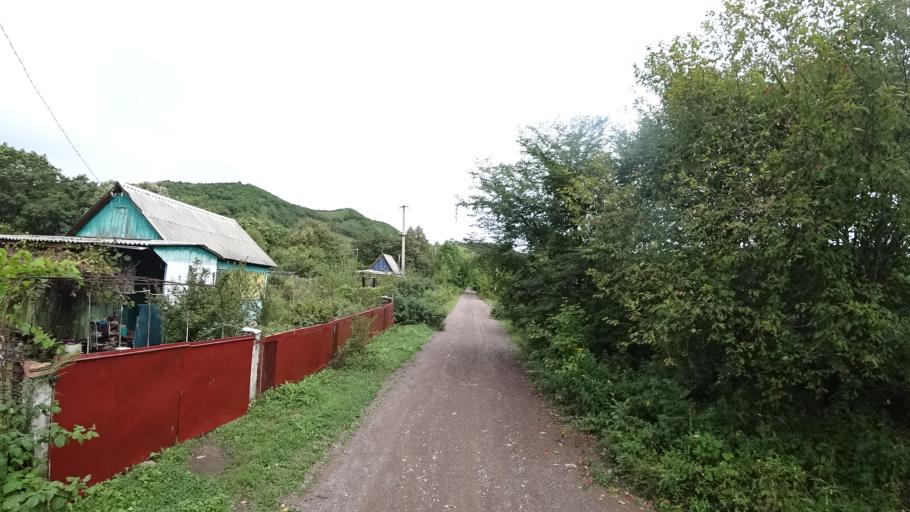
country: RU
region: Primorskiy
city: Monastyrishche
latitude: 44.1657
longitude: 132.5403
